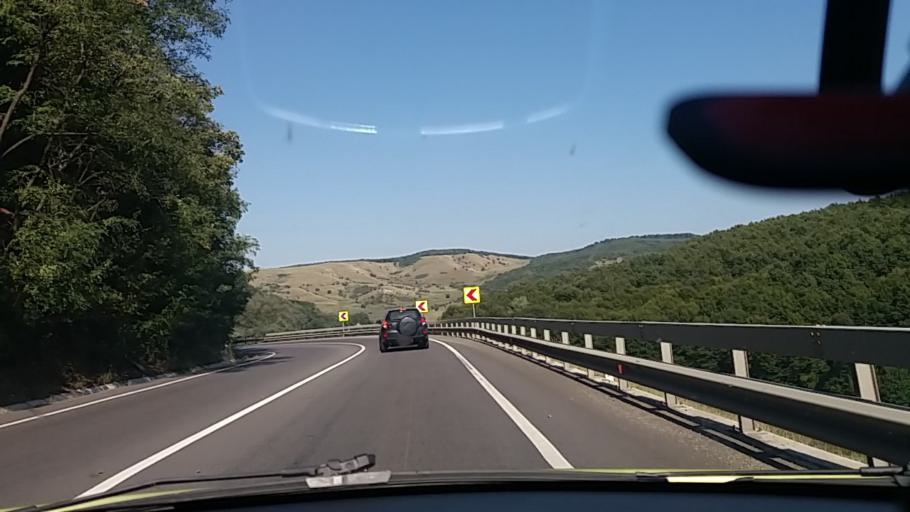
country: RO
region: Sibiu
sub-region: Comuna Slimnic
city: Slimnic
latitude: 45.9413
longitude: 24.1705
